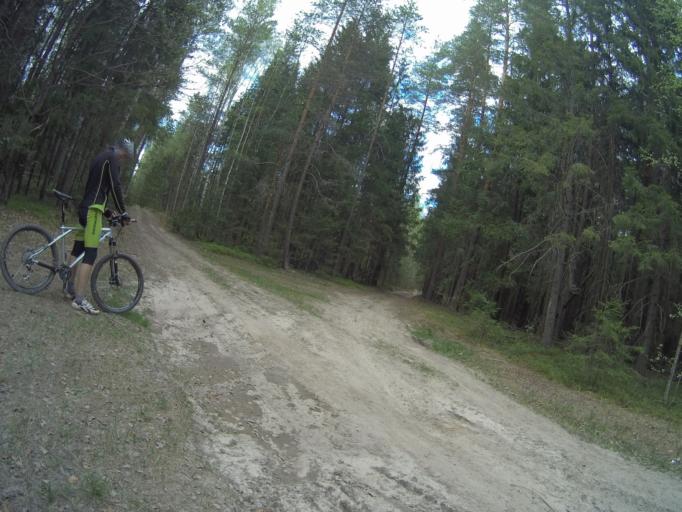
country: RU
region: Vladimir
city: Orgtrud
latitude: 56.1151
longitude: 40.7116
